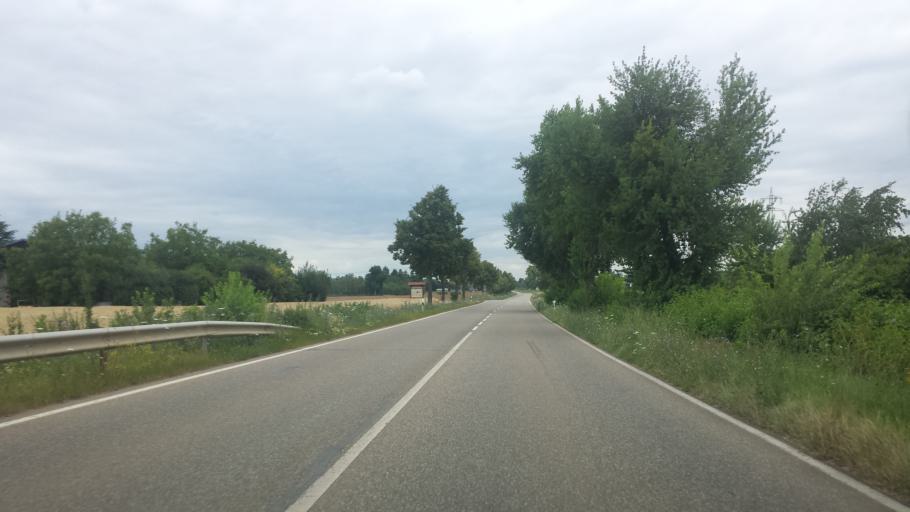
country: DE
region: Rheinland-Pfalz
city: Meckenheim
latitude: 49.3851
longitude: 8.2482
